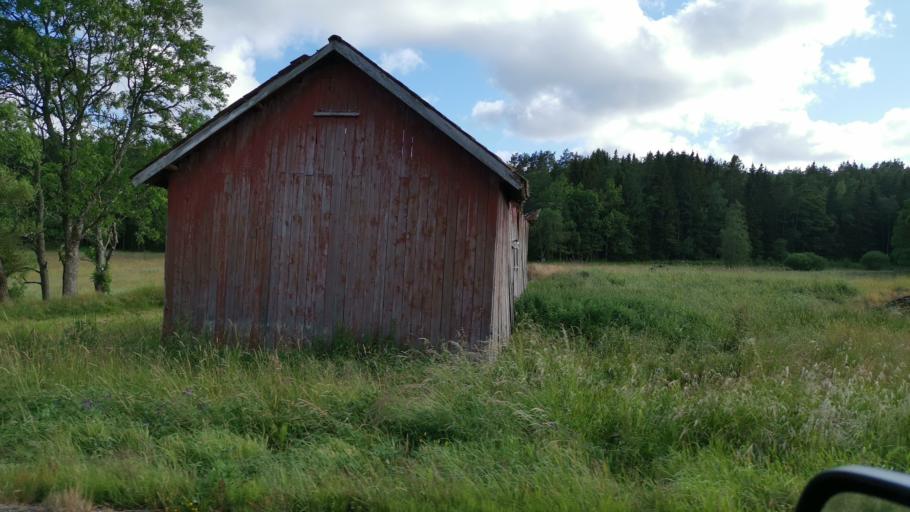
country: SE
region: Vaestra Goetaland
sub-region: Orust
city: Henan
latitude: 58.1619
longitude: 11.6135
